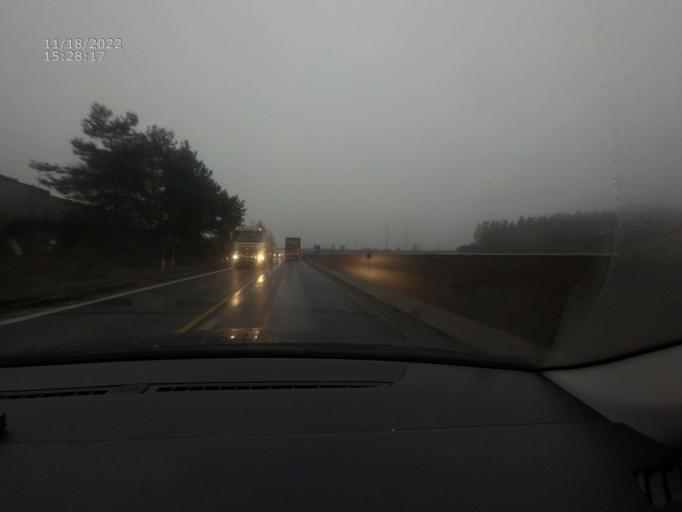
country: CZ
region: Central Bohemia
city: Milin
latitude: 49.6346
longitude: 14.0516
